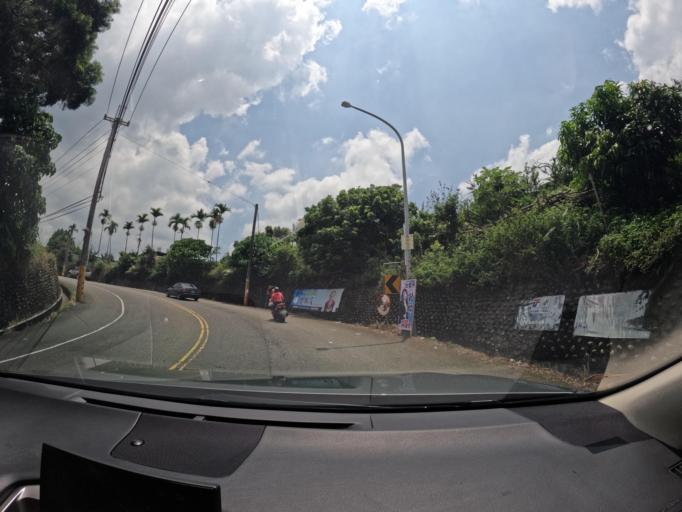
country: TW
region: Taiwan
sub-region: Nantou
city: Nantou
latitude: 23.8536
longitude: 120.6272
